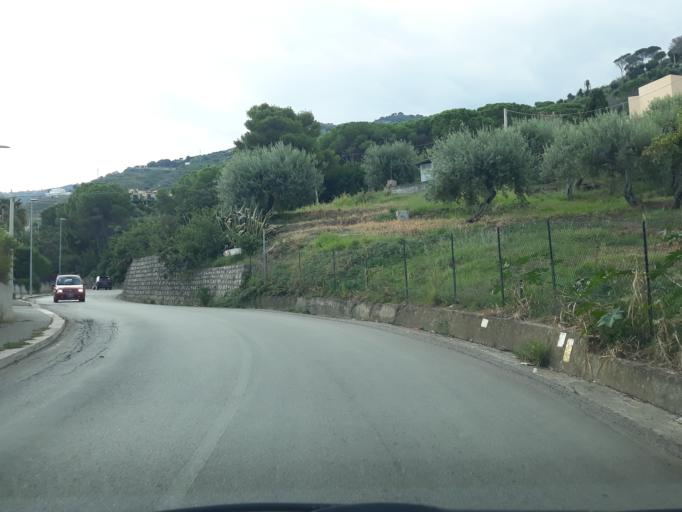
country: IT
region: Sicily
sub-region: Palermo
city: Cefalu
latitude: 38.0306
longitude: 14.0011
